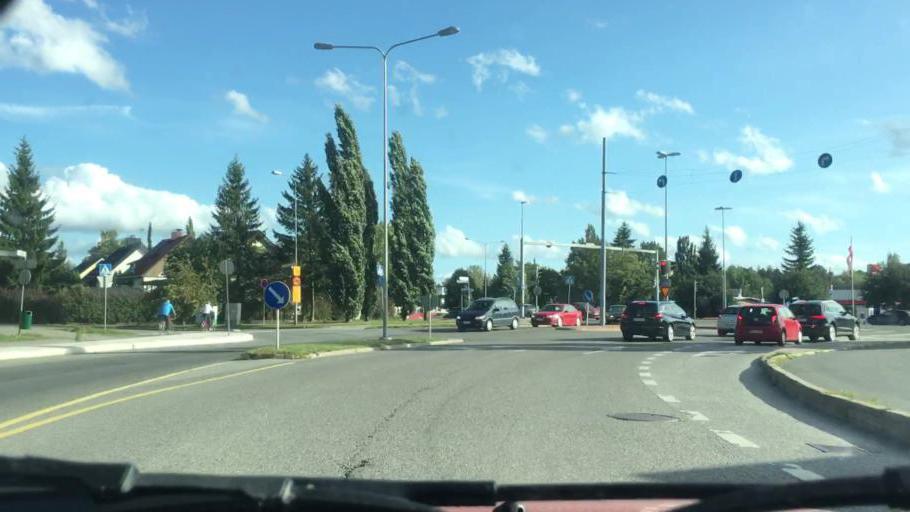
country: FI
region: Varsinais-Suomi
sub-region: Turku
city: Turku
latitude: 60.4706
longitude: 22.2352
